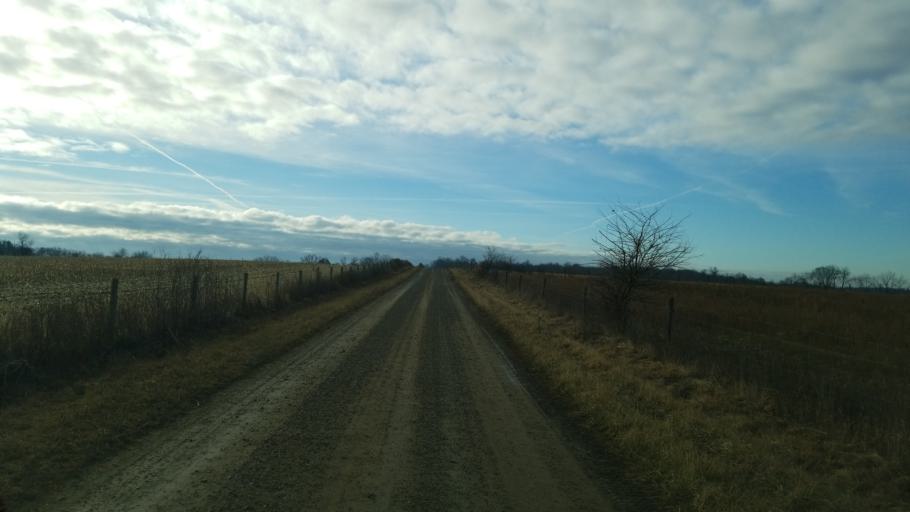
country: US
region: Ohio
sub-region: Knox County
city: Gambier
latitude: 40.3214
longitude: -82.3210
